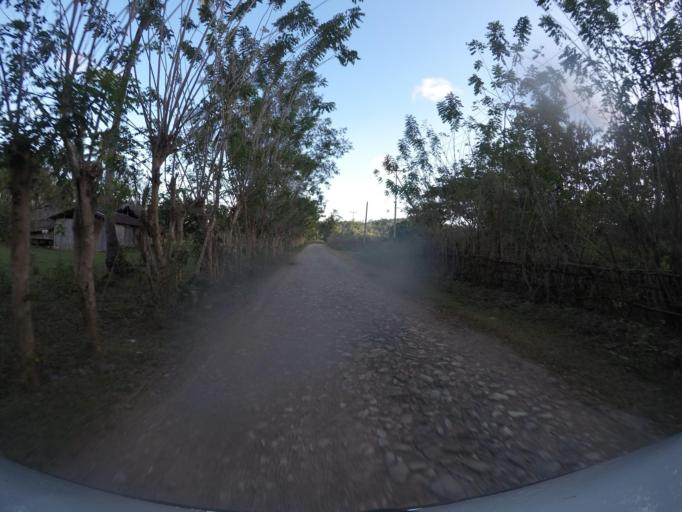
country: TL
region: Baucau
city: Venilale
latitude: -8.7269
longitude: 126.7086
